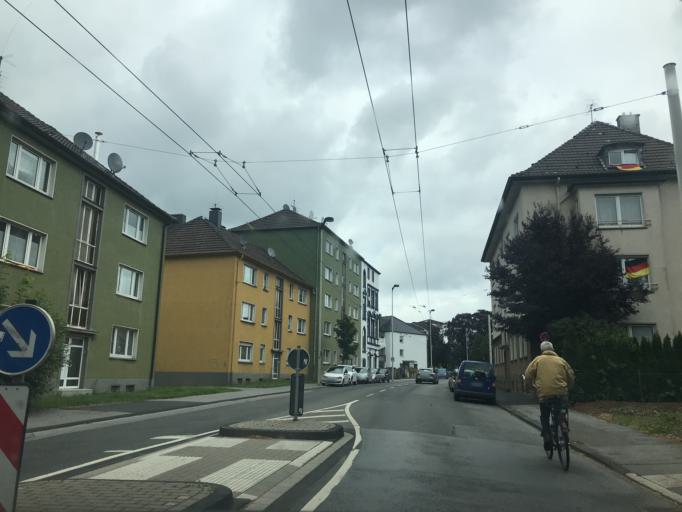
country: DE
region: North Rhine-Westphalia
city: Haan
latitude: 51.1601
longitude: 7.0084
